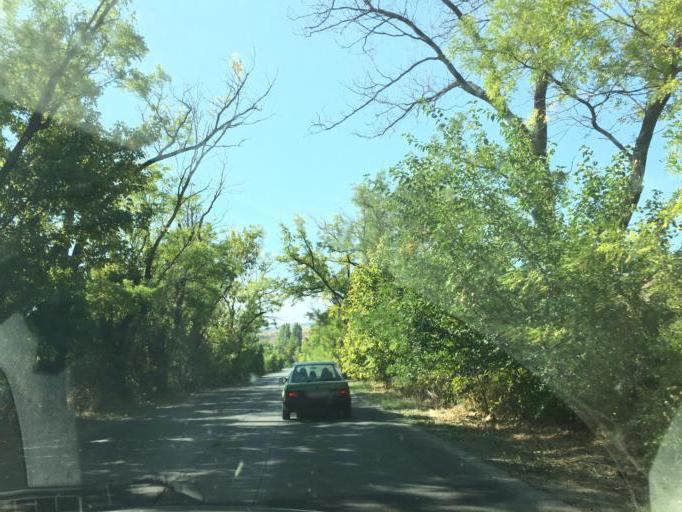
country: BG
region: Pazardzhik
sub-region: Obshtina Pazardzhik
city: Pazardzhik
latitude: 42.1259
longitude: 24.2939
